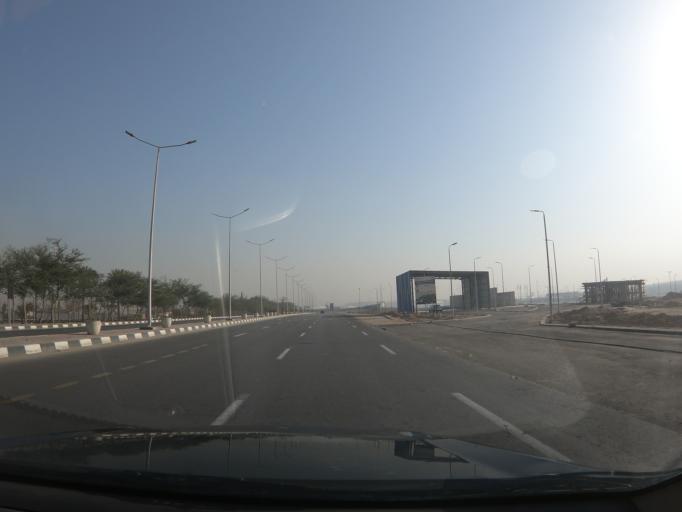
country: EG
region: Muhafazat al Qalyubiyah
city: Al Khankah
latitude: 30.0995
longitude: 31.3860
